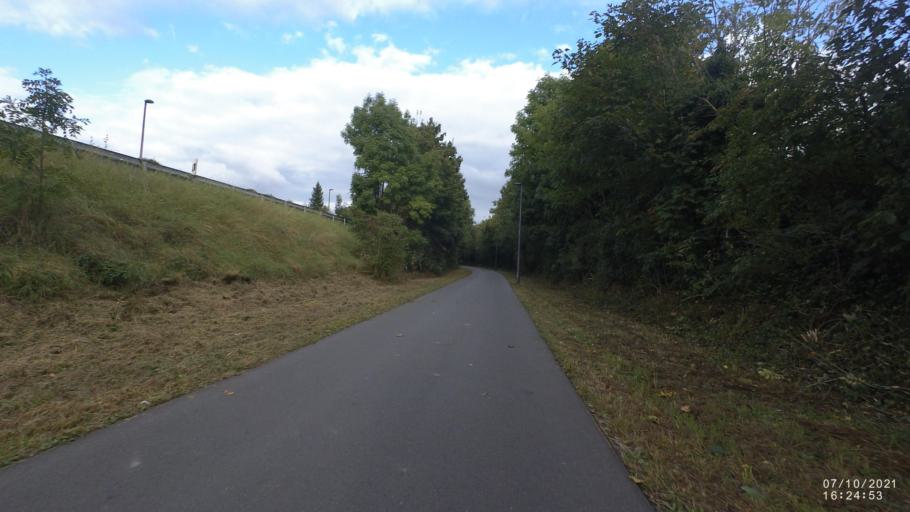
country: DE
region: North Rhine-Westphalia
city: Hemer
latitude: 51.3915
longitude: 7.7685
